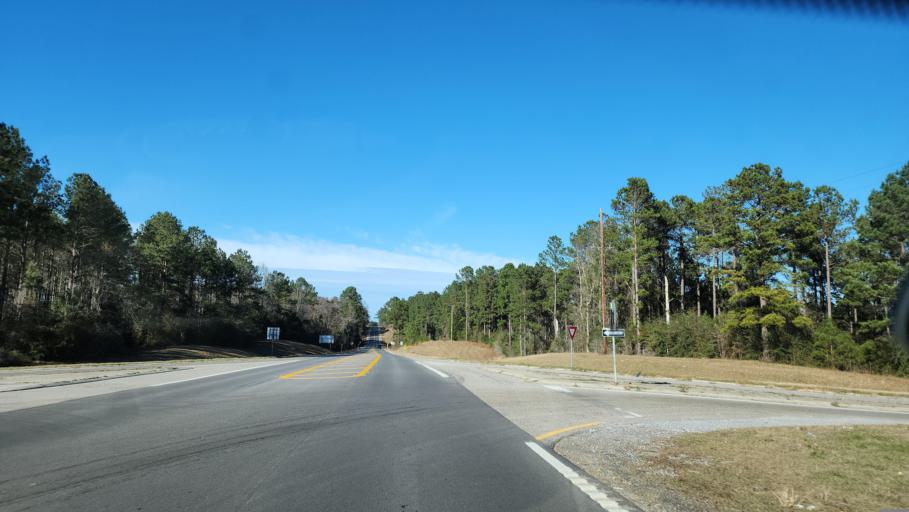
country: US
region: Mississippi
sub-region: Wayne County
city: Waynesboro
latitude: 31.7054
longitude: -88.6442
